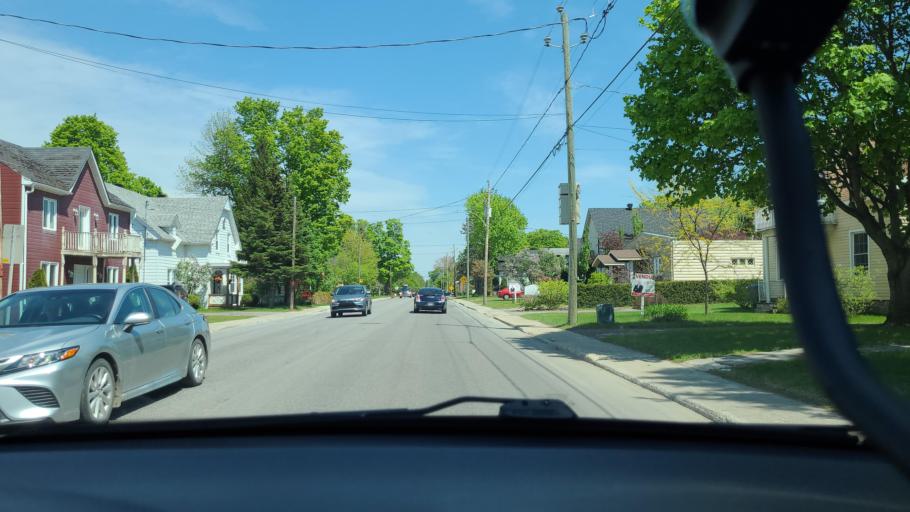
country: CA
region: Quebec
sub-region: Laurentides
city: Lachute
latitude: 45.6580
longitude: -74.3293
